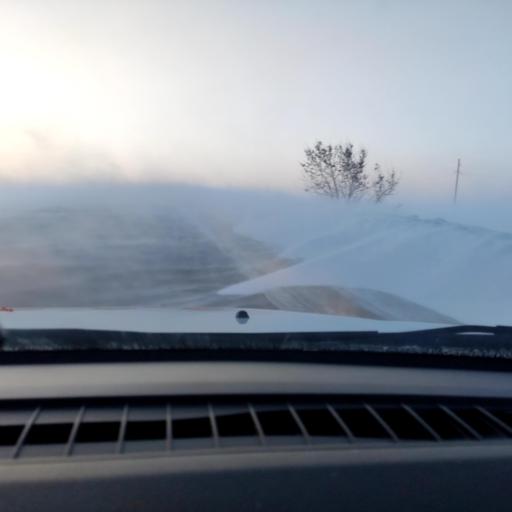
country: RU
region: Samara
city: Georgiyevka
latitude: 53.4165
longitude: 50.8716
